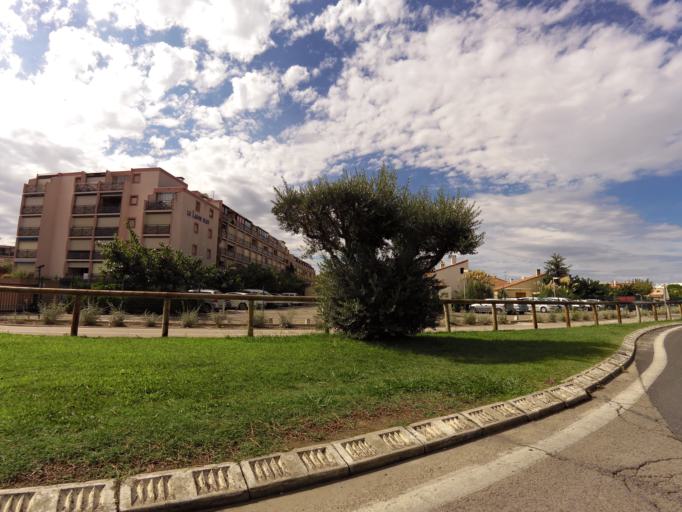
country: FR
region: Languedoc-Roussillon
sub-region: Departement du Gard
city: Le Grau-du-Roi
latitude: 43.5262
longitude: 4.1493
